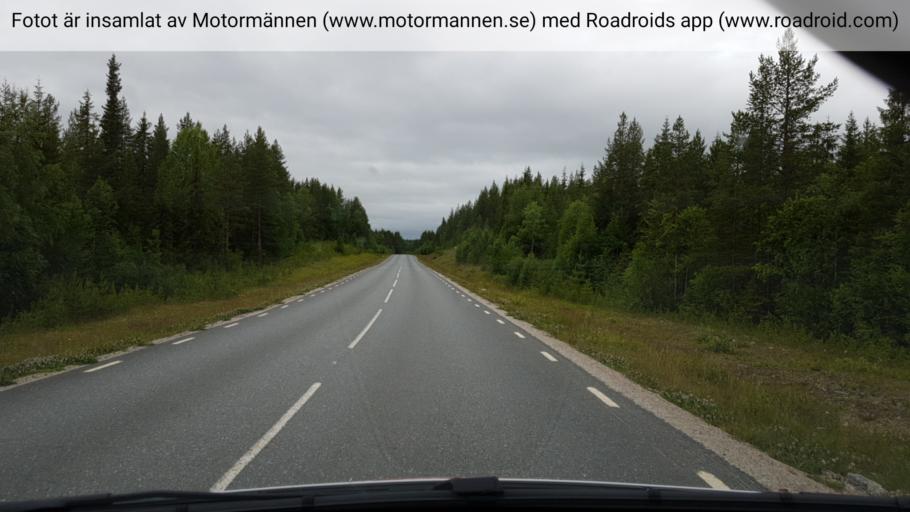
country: SE
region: Vaesterbotten
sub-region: Lycksele Kommun
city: Lycksele
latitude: 64.5066
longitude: 18.9154
